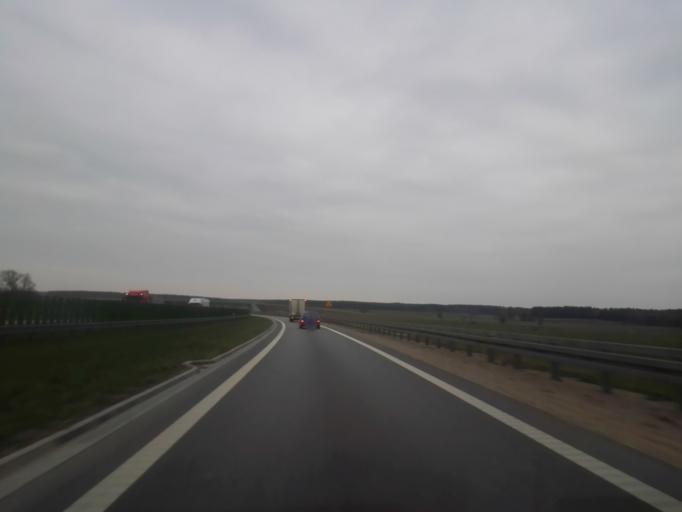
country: PL
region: Podlasie
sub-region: Powiat kolnenski
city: Stawiski
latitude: 53.3775
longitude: 22.1431
